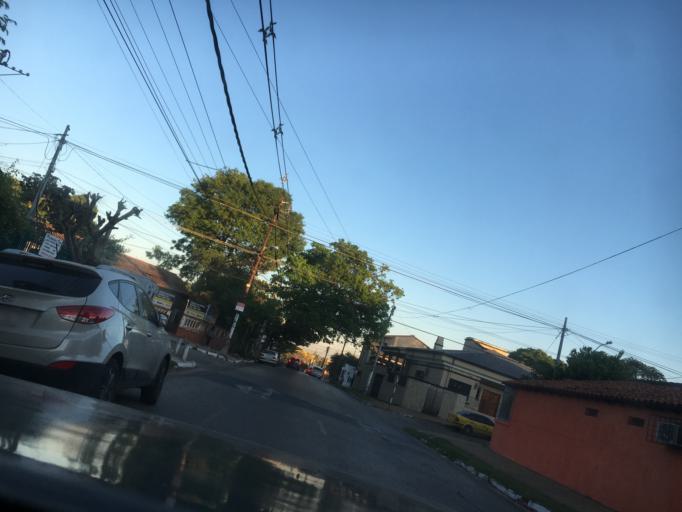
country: PY
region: Asuncion
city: Asuncion
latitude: -25.3129
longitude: -57.6211
